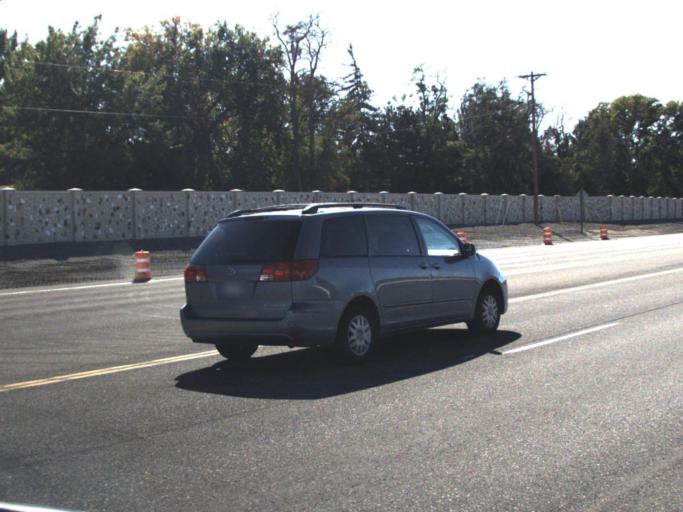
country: US
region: Washington
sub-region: Benton County
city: Richland
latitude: 46.2909
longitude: -119.3059
